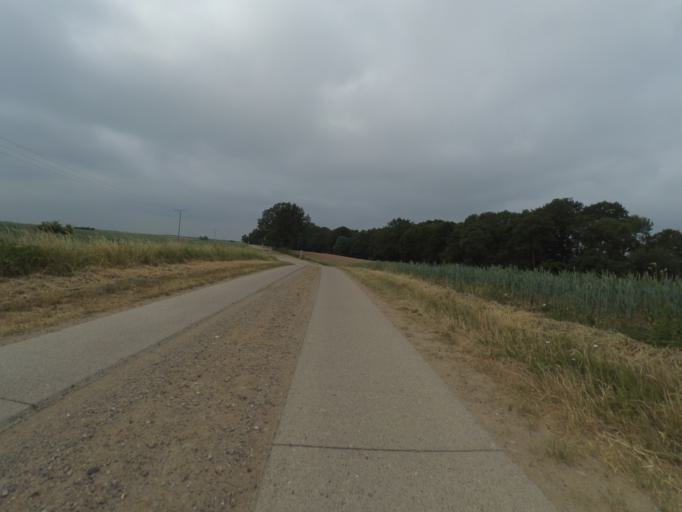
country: DE
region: Mecklenburg-Vorpommern
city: Goldberg
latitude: 53.5183
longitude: 12.0941
